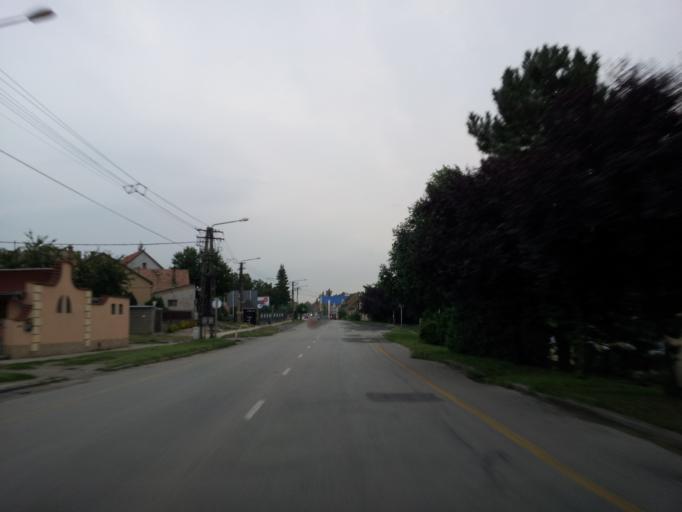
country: HU
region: Tolna
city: Tolna
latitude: 46.4225
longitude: 18.7796
